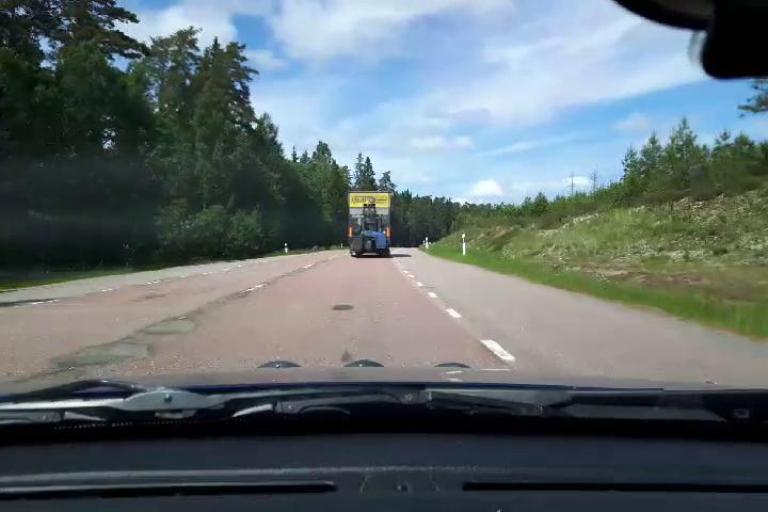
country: SE
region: Uppsala
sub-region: Osthammars Kommun
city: Bjorklinge
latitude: 60.1228
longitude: 17.5098
